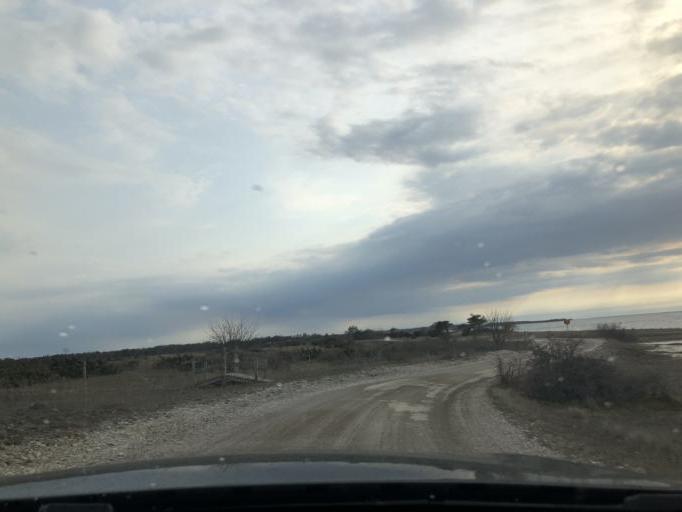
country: SE
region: Kalmar
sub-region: Borgholms Kommun
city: Borgholm
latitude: 57.2220
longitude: 16.9525
